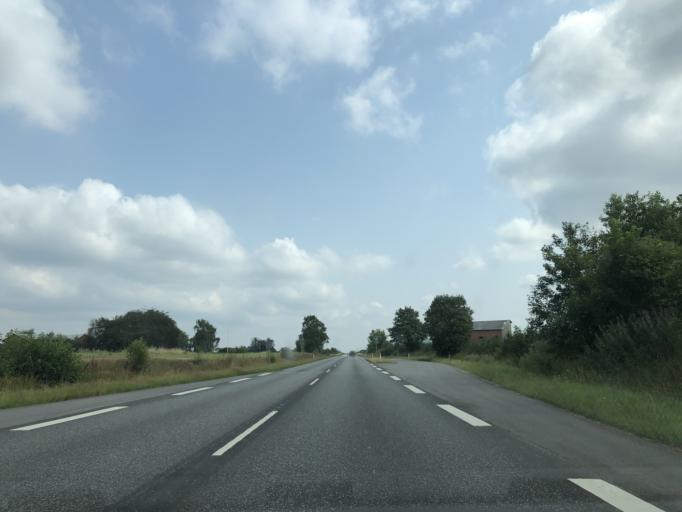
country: DK
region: Central Jutland
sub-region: Silkeborg Kommune
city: Kjellerup
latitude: 56.3328
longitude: 9.5455
